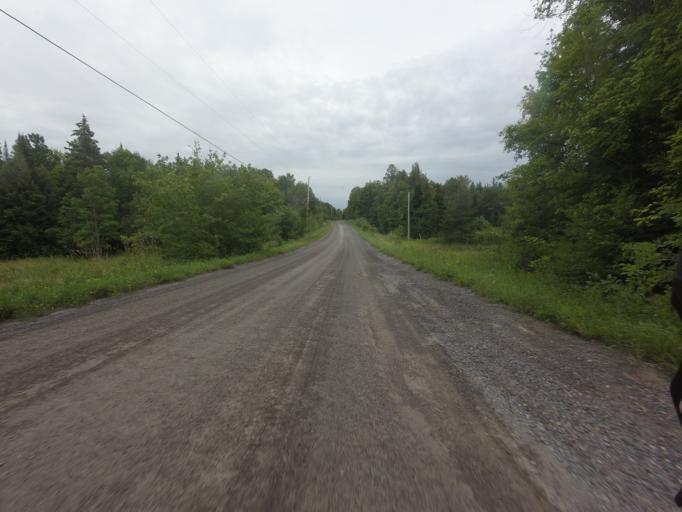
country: CA
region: Ontario
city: Carleton Place
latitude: 45.1683
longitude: -76.2786
